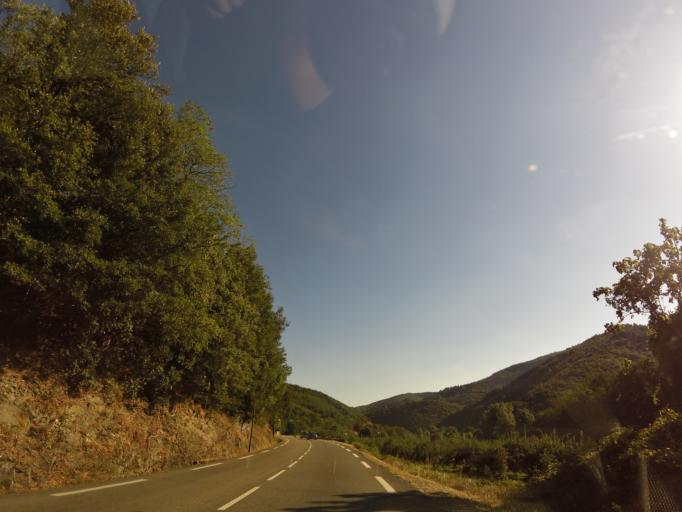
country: FR
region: Languedoc-Roussillon
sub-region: Departement du Gard
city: Sumene
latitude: 43.9908
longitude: 3.6886
